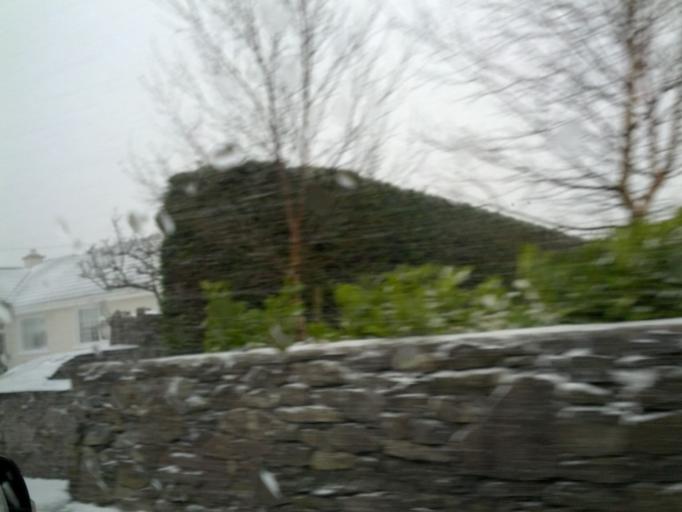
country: IE
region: Connaught
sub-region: County Galway
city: Oranmore
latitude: 53.1952
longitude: -8.8933
